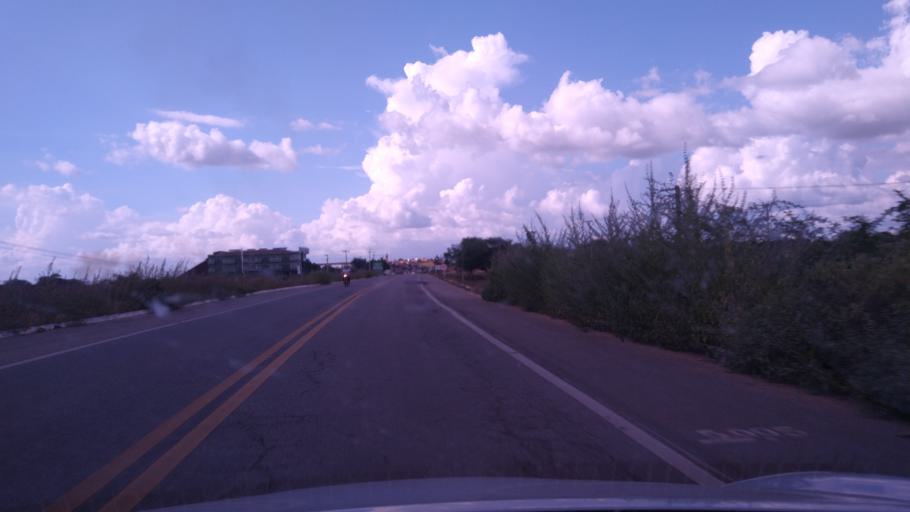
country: BR
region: Ceara
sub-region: Caninde
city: Caninde
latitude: -4.3855
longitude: -39.3122
